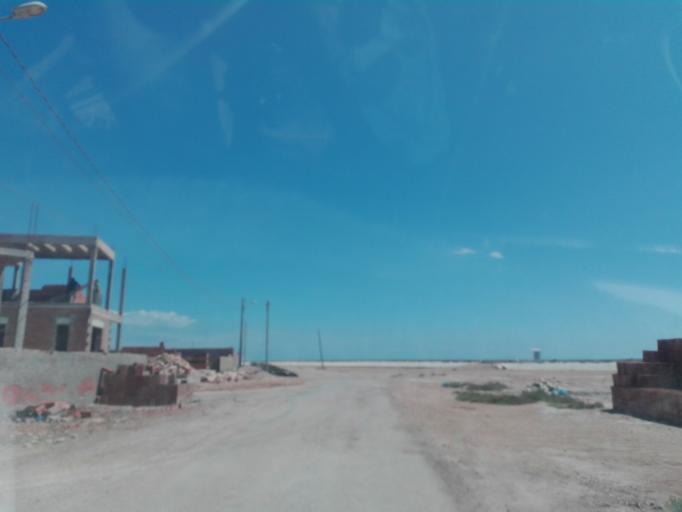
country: TN
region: Safaqis
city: Jabinyanah
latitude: 34.8180
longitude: 11.2635
